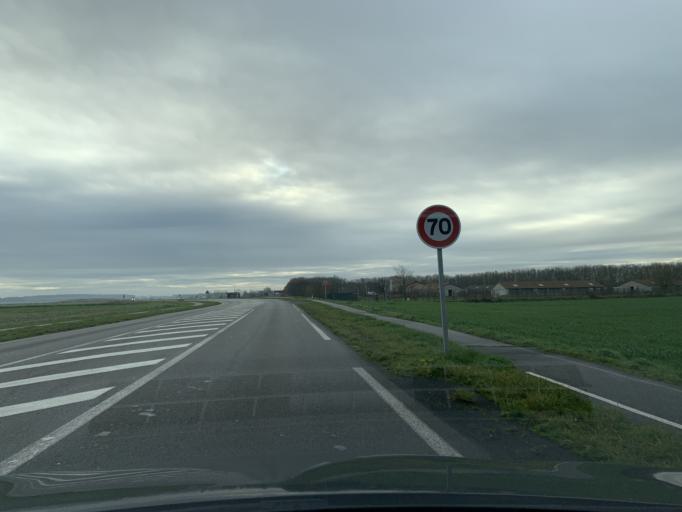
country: FR
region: Nord-Pas-de-Calais
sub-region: Departement du Nord
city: Goeulzin
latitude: 50.3317
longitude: 3.1048
